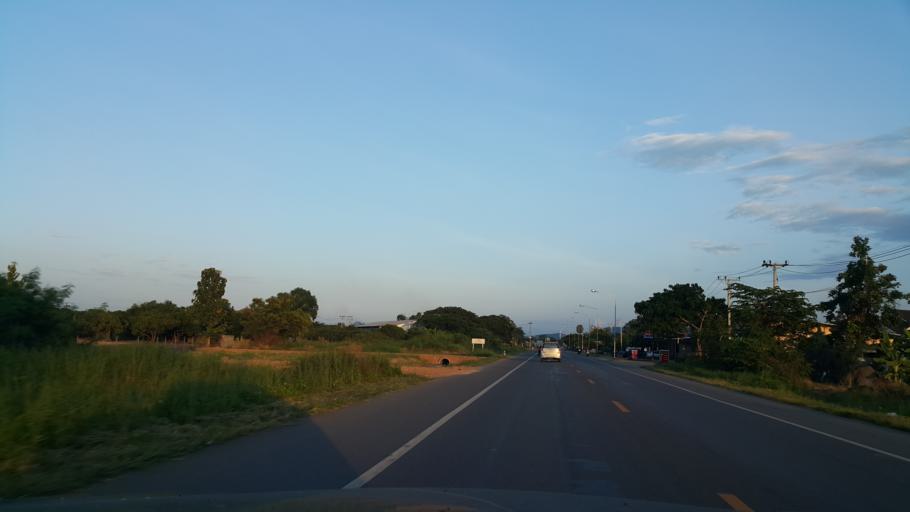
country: TH
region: Lamphun
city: Pa Sang
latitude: 18.4877
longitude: 98.9294
